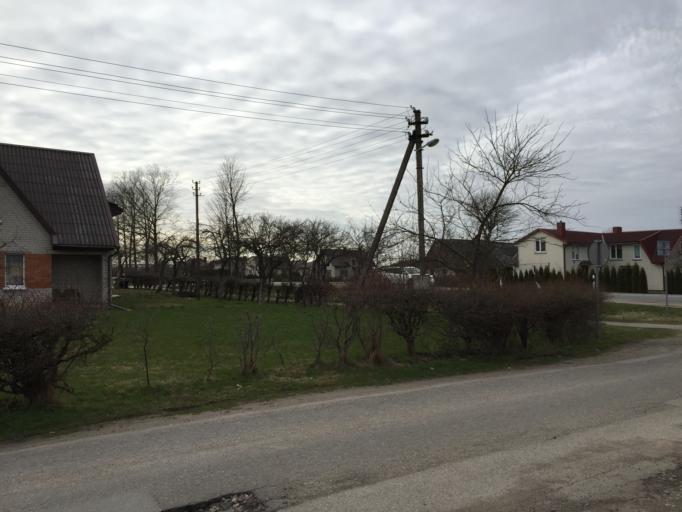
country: LT
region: Klaipedos apskritis
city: Gargzdai
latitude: 55.7163
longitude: 21.3068
